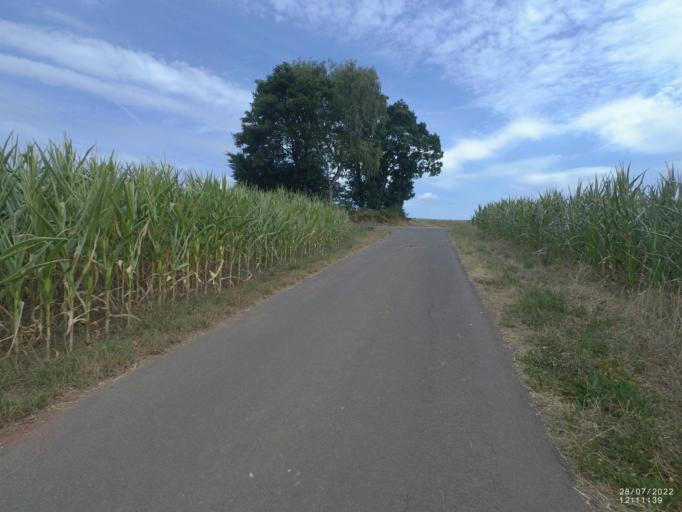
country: DE
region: Rheinland-Pfalz
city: Oberbettingen
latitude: 50.2568
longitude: 6.6290
